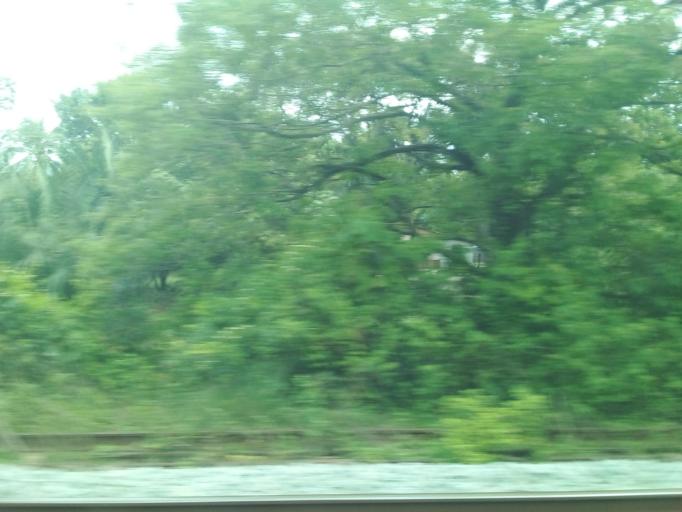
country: BR
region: Maranhao
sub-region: Arari
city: Arari
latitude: -3.5689
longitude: -44.7783
